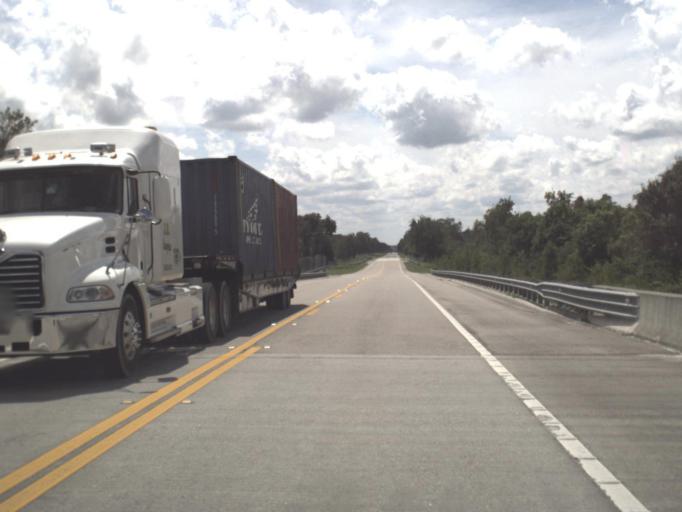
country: US
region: Florida
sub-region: Collier County
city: Immokalee
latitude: 26.2458
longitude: -81.3422
